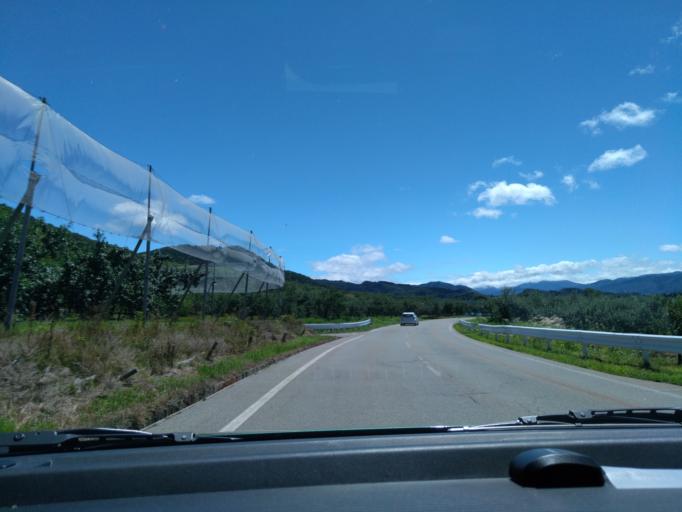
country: JP
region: Akita
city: Yuzawa
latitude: 39.2204
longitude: 140.5666
